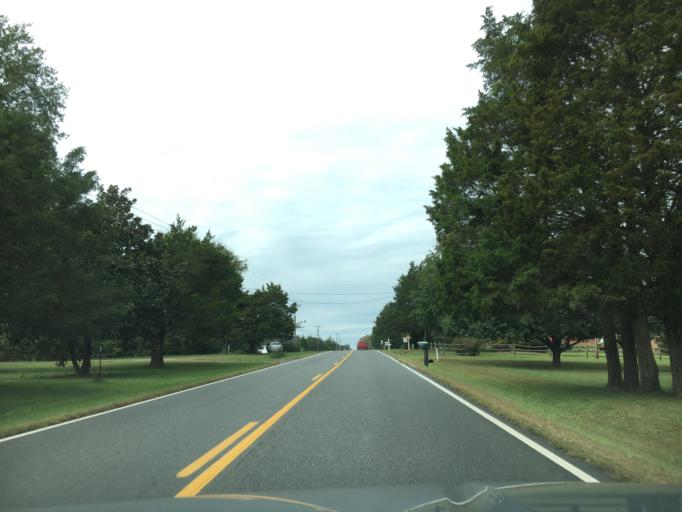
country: US
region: Virginia
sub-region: Goochland County
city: Goochland
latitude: 37.7491
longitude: -77.8574
